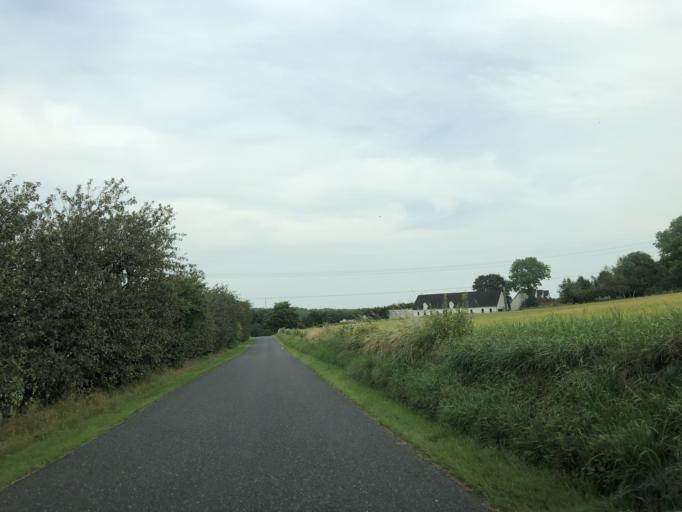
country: DK
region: Central Jutland
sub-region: Viborg Kommune
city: Viborg
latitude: 56.4873
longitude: 9.5176
